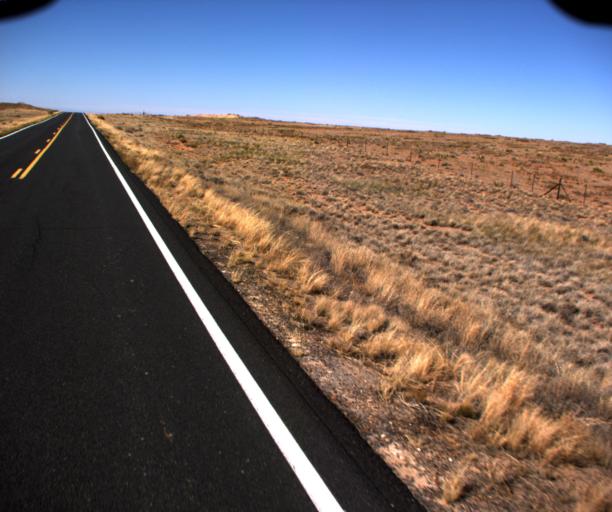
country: US
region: Arizona
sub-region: Coconino County
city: Tuba City
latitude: 35.9919
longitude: -111.0155
